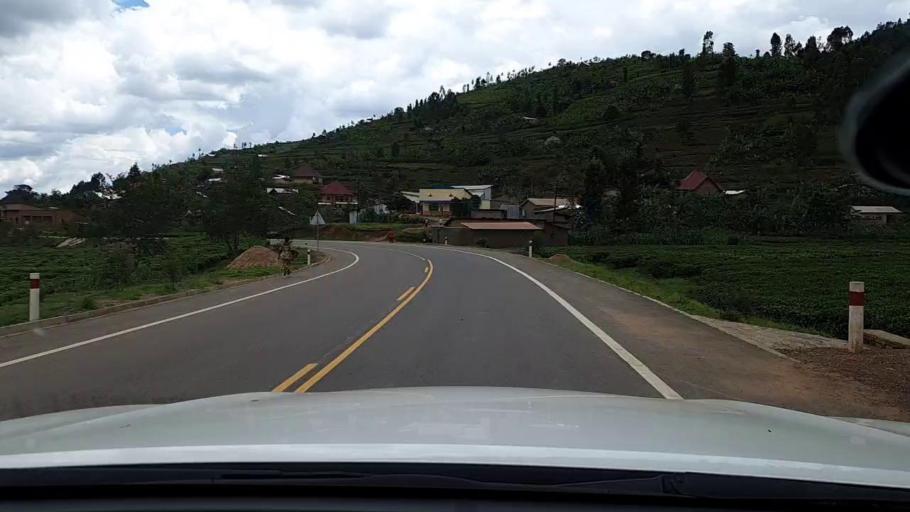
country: RW
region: Northern Province
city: Byumba
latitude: -1.6527
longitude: 29.9034
